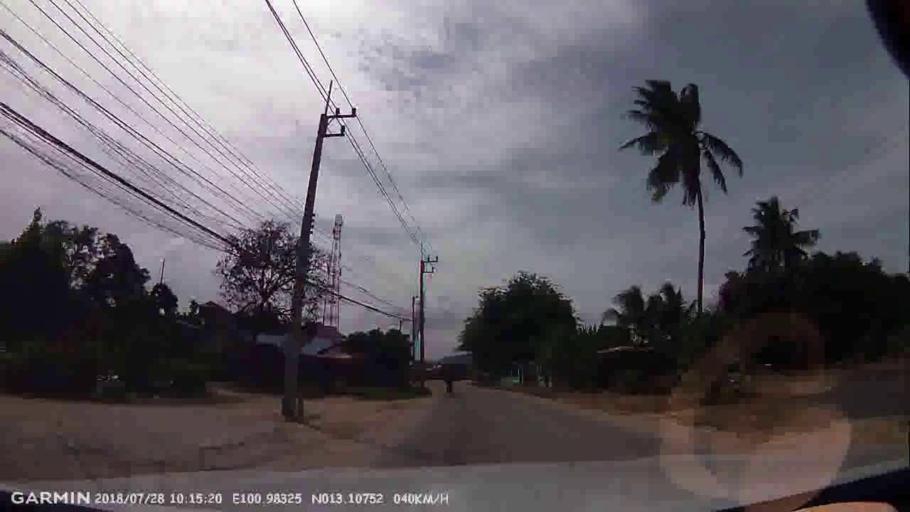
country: TH
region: Chon Buri
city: Ban Talat Bueng
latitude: 13.1075
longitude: 100.9834
